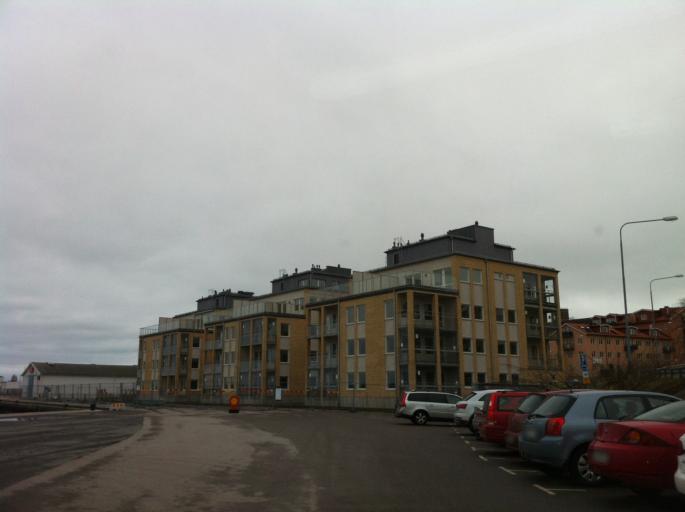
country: SE
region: Kalmar
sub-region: Vasterviks Kommun
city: Vaestervik
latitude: 57.7967
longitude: 16.6194
